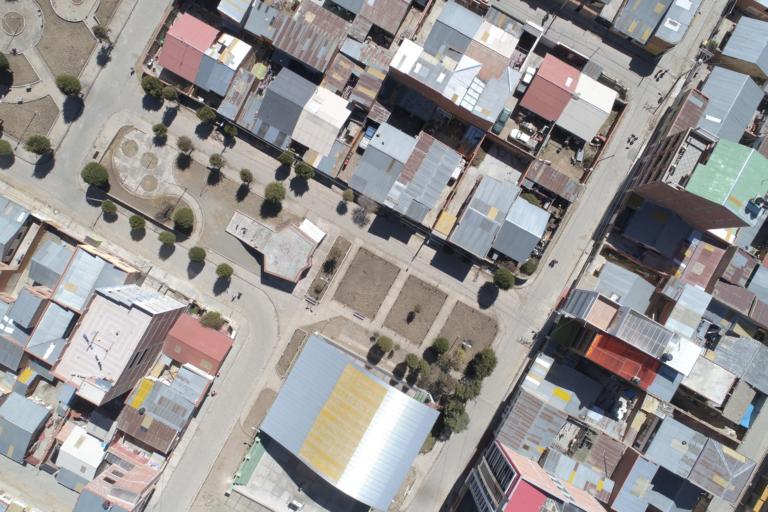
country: BO
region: La Paz
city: La Paz
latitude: -16.5246
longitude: -68.1528
